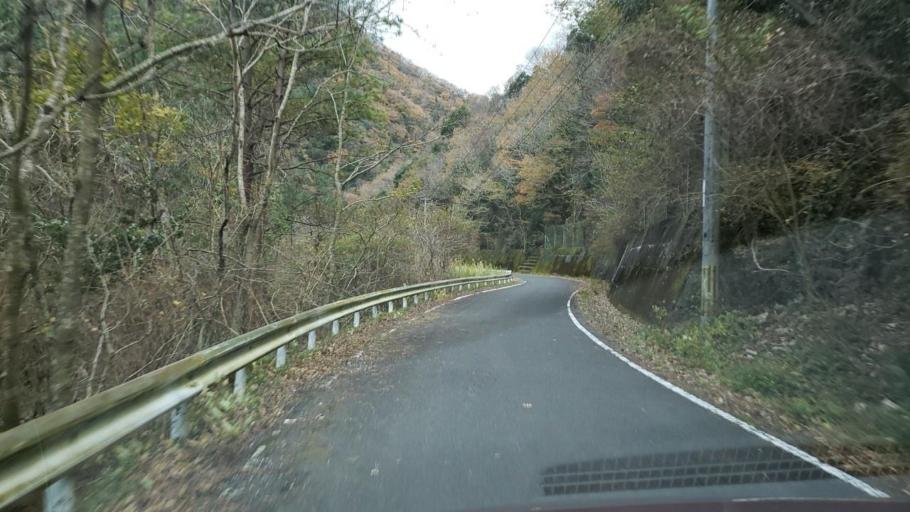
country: JP
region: Tokushima
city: Wakimachi
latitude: 34.1362
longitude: 134.2296
